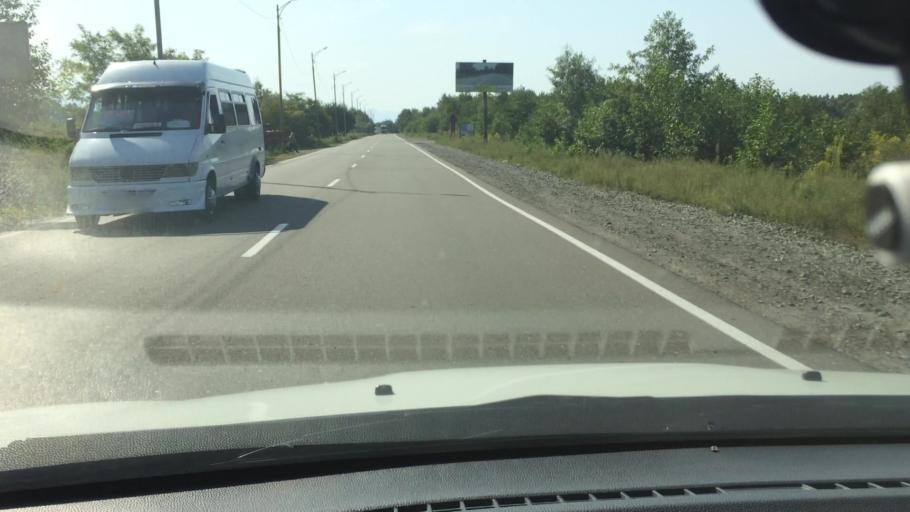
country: GE
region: Guria
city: Urek'i
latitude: 41.9642
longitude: 41.7732
